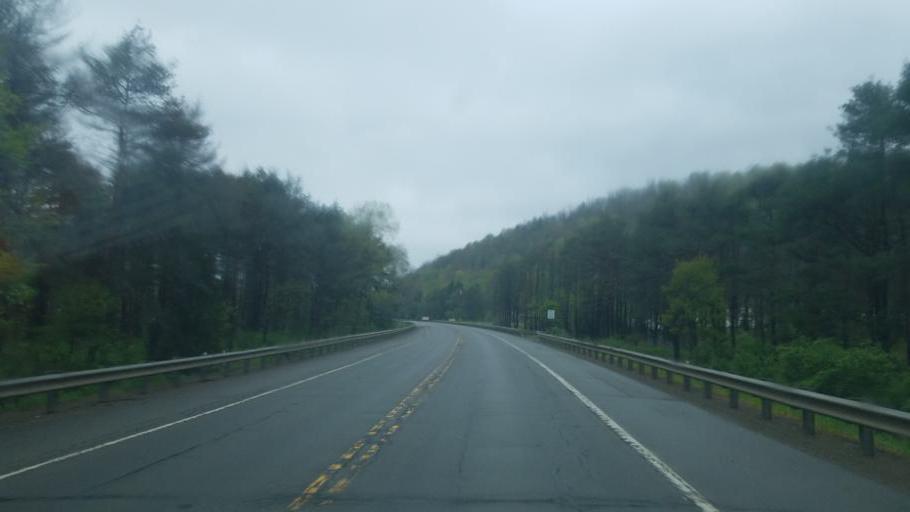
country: US
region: Pennsylvania
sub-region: Potter County
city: Coudersport
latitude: 41.7815
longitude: -78.1495
